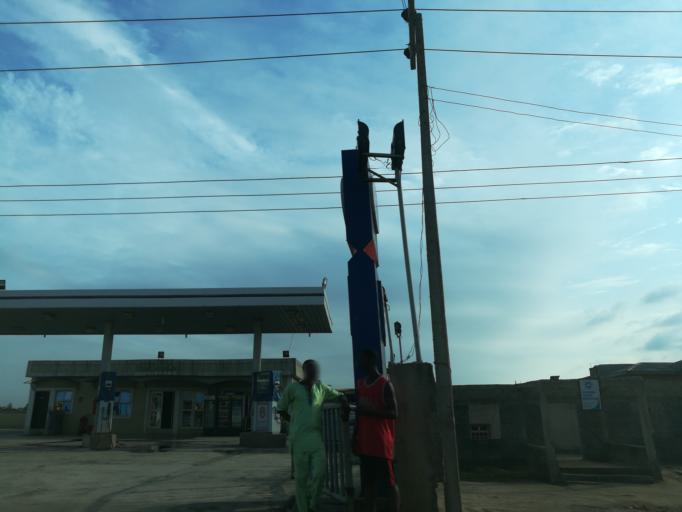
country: NG
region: Lagos
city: Ebute Ikorodu
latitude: 6.6132
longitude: 3.4790
